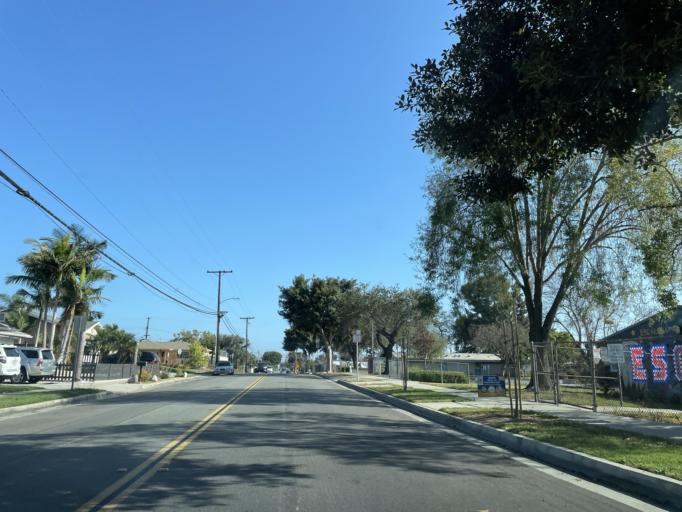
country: US
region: California
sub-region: Los Angeles County
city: La Mirada
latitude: 33.8939
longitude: -118.0117
